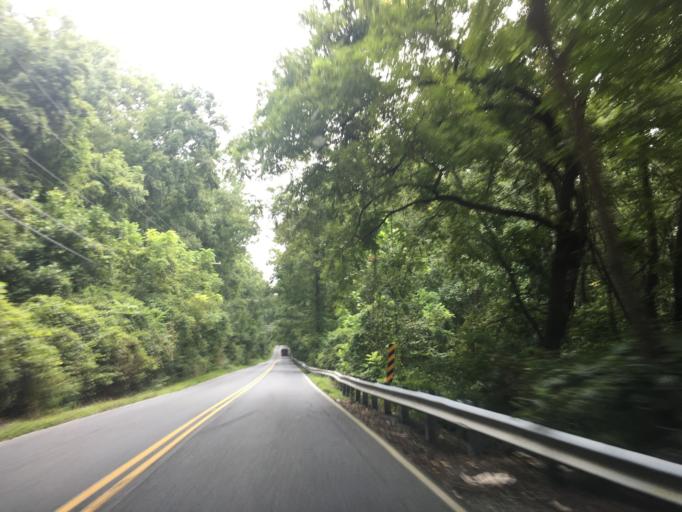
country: US
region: Maryland
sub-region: Anne Arundel County
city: Crownsville
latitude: 39.0421
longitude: -76.5862
